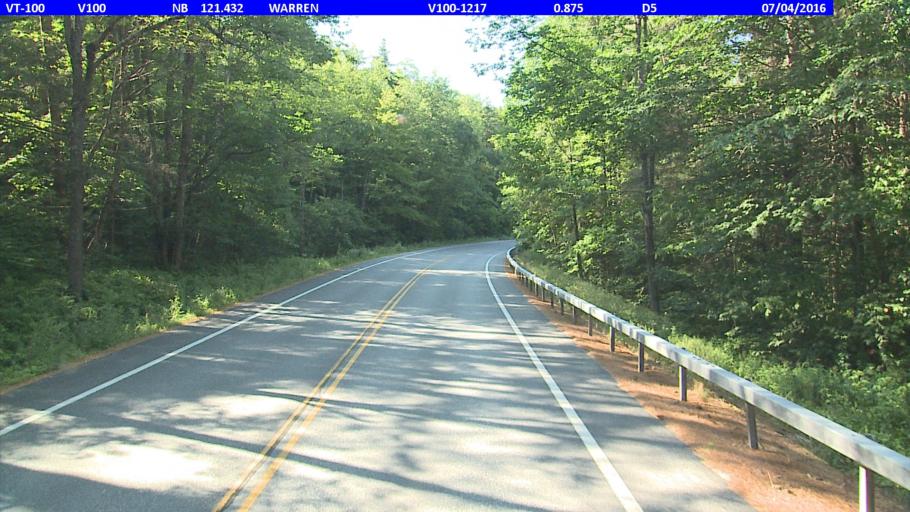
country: US
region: Vermont
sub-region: Washington County
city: Northfield
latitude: 44.0722
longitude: -72.8602
